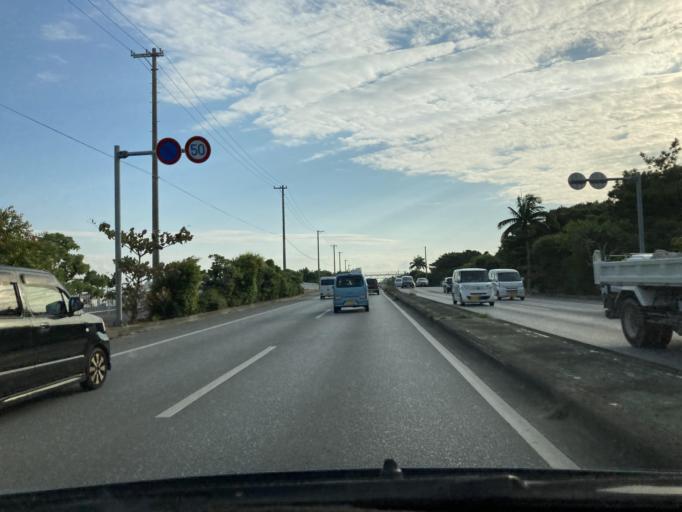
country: JP
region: Okinawa
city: Okinawa
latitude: 26.3270
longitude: 127.8350
